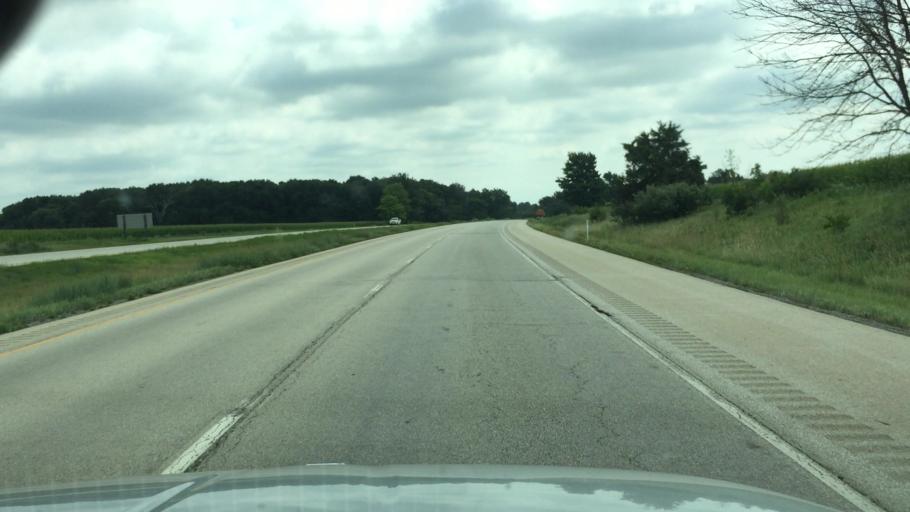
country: US
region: Illinois
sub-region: Knox County
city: Knoxville
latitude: 40.9185
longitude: -90.2650
